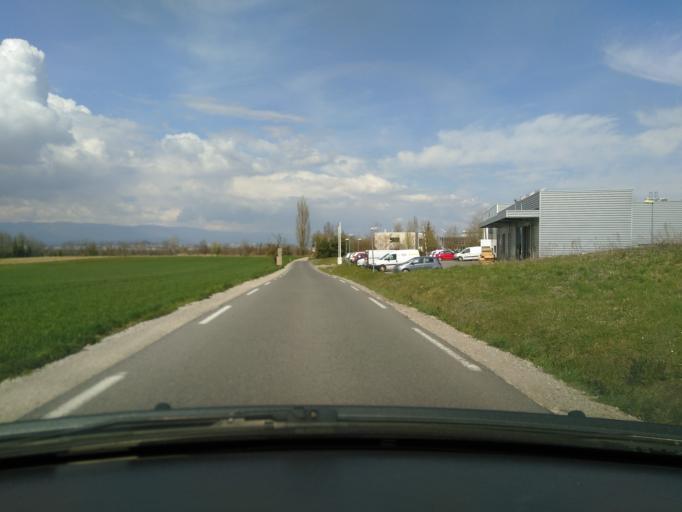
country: FR
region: Rhone-Alpes
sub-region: Departement de la Haute-Savoie
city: Archamps
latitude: 46.1379
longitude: 6.1141
